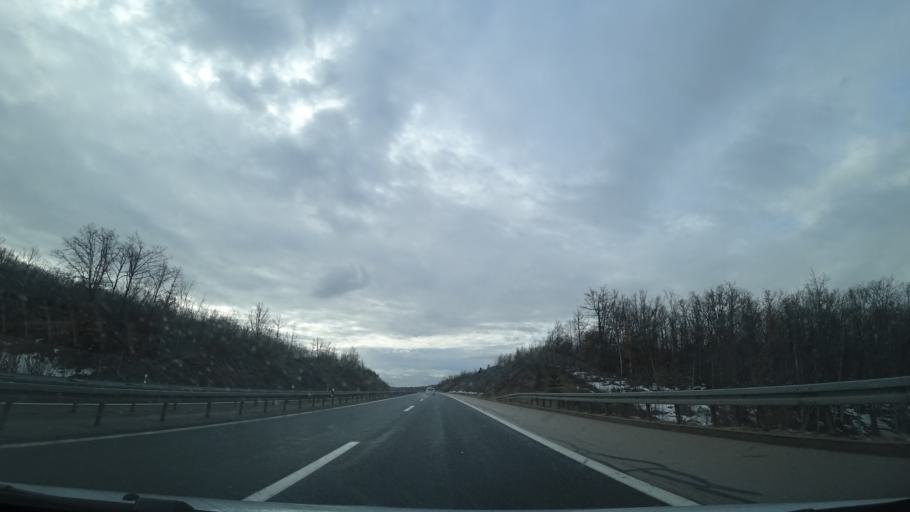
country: HR
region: Licko-Senjska
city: Gospic
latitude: 44.7102
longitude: 15.3885
